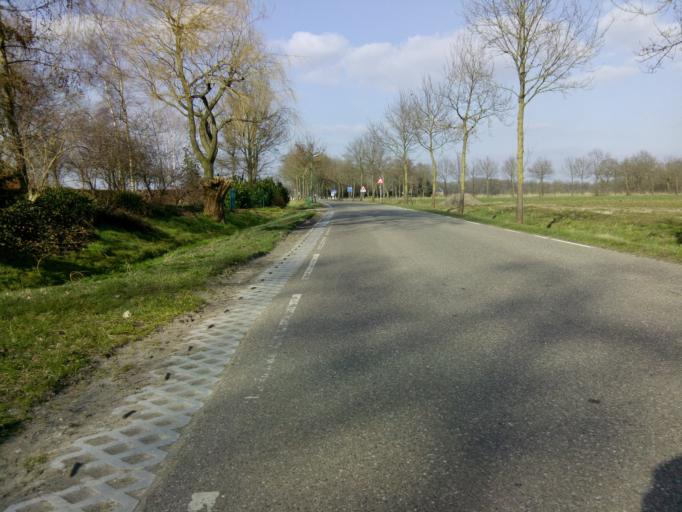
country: NL
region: Utrecht
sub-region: Gemeente Leusden
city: Leusden
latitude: 52.1042
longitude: 5.4544
